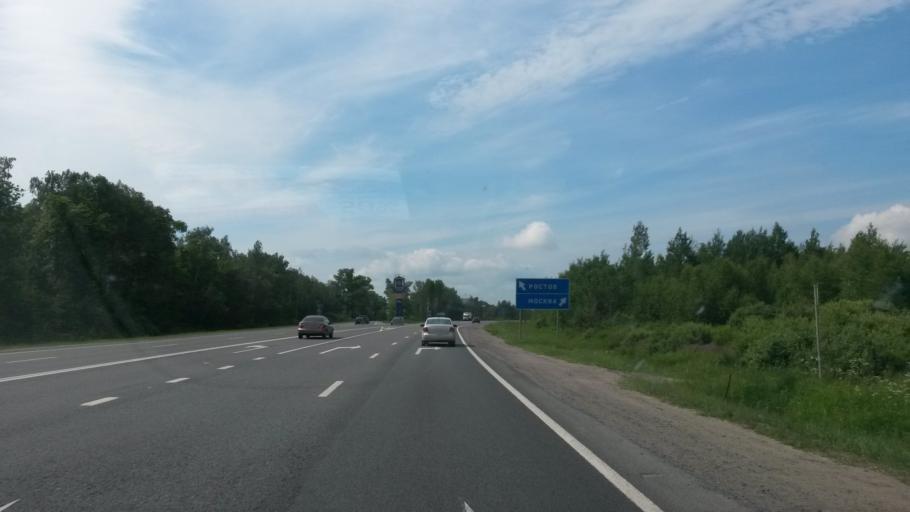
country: RU
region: Jaroslavl
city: Rostov
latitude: 57.2207
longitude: 39.4600
